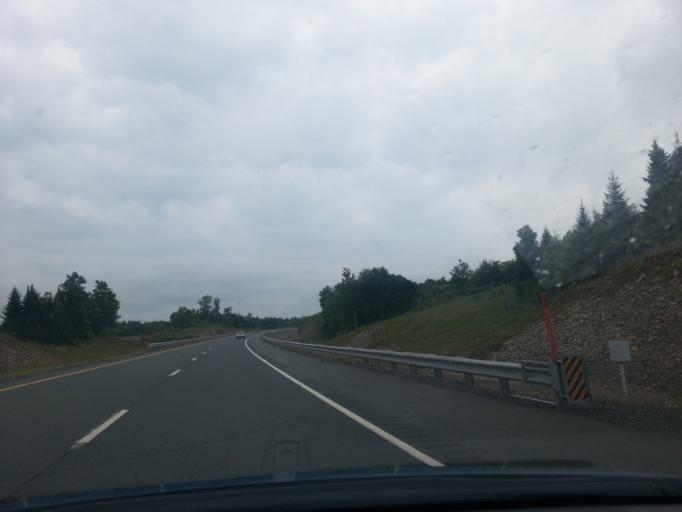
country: US
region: Maine
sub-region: Aroostook County
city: Easton
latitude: 46.6235
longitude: -67.7391
